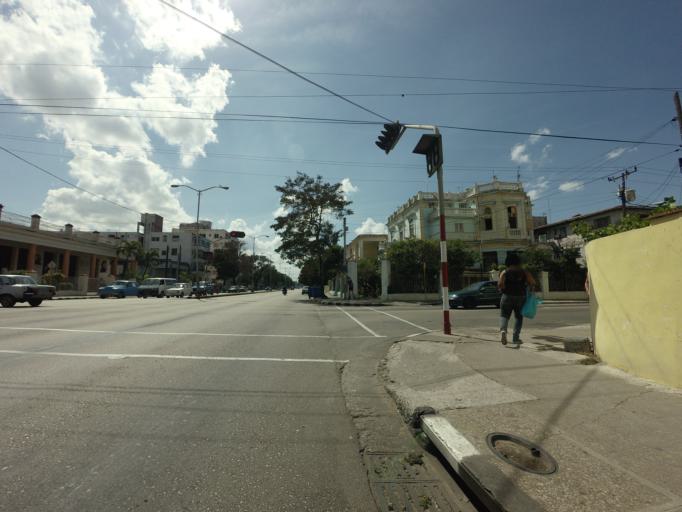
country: CU
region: La Habana
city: Havana
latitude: 23.1332
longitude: -82.4049
